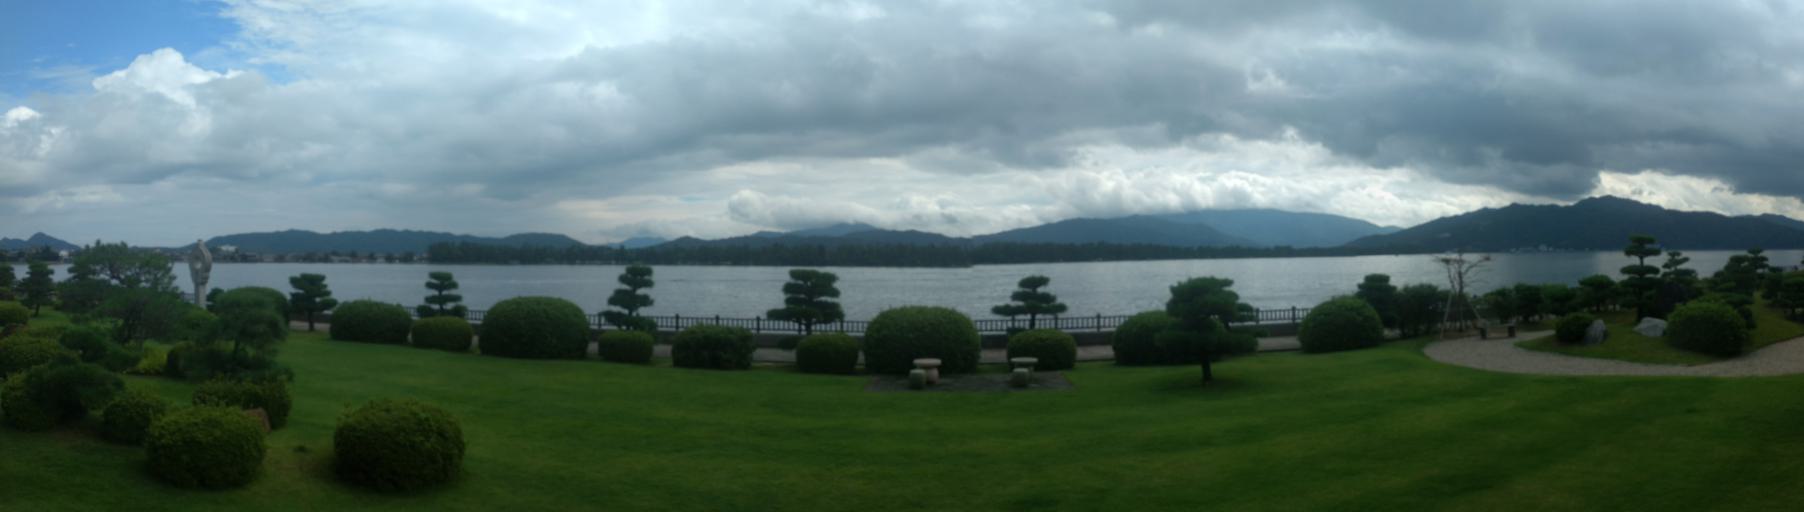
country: JP
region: Kyoto
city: Miyazu
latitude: 35.5802
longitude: 135.1908
